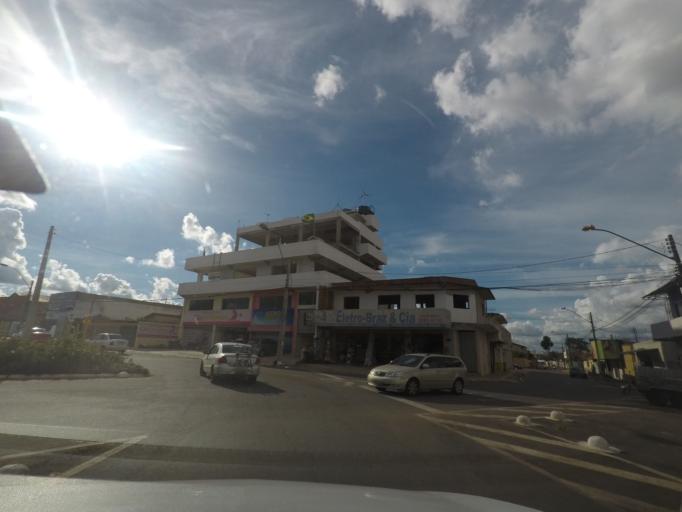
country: BR
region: Goias
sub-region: Goiania
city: Goiania
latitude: -16.7211
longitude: -49.3033
